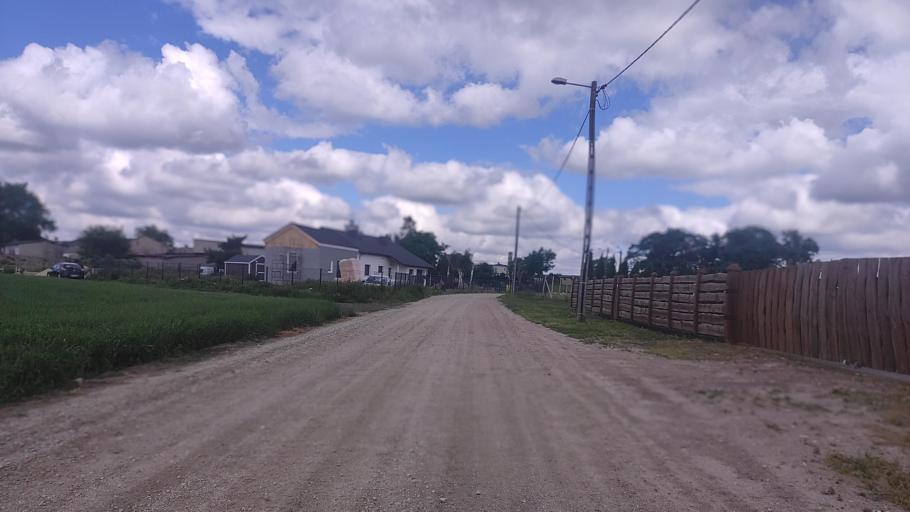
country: PL
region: Greater Poland Voivodeship
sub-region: Powiat poznanski
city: Kostrzyn
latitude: 52.4134
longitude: 17.1739
